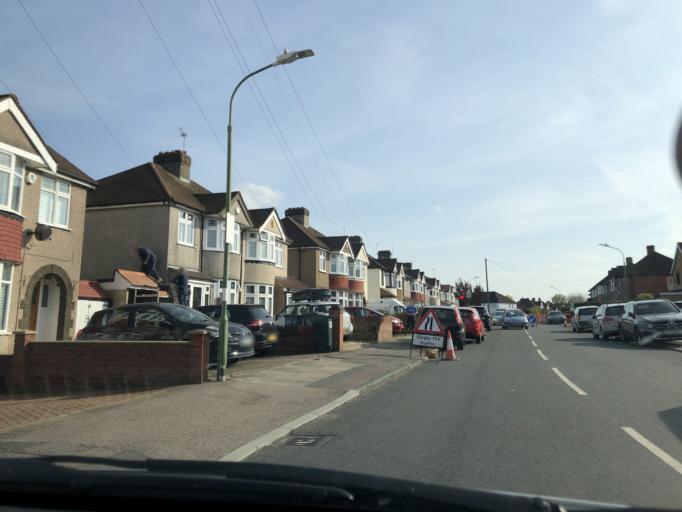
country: GB
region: England
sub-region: Kent
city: Dartford
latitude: 51.4439
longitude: 0.1859
